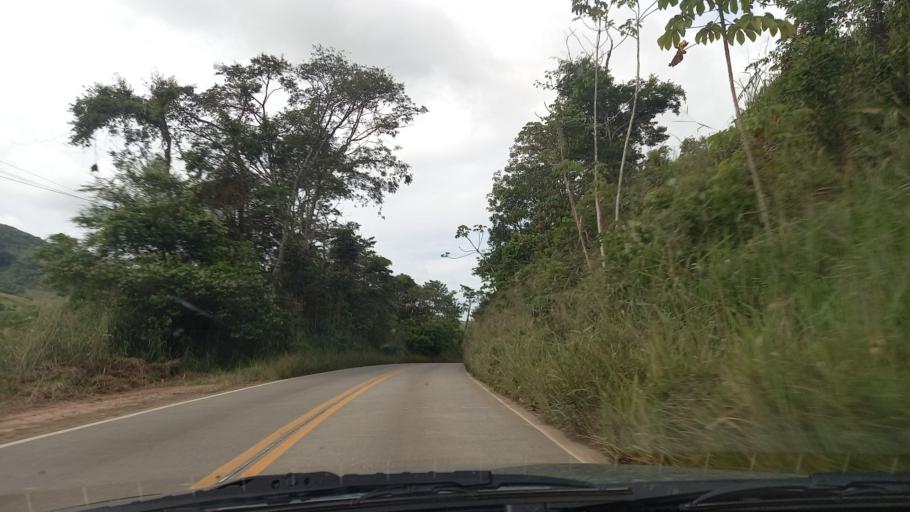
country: BR
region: Pernambuco
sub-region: Maraial
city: Maraial
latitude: -8.7628
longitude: -35.8602
